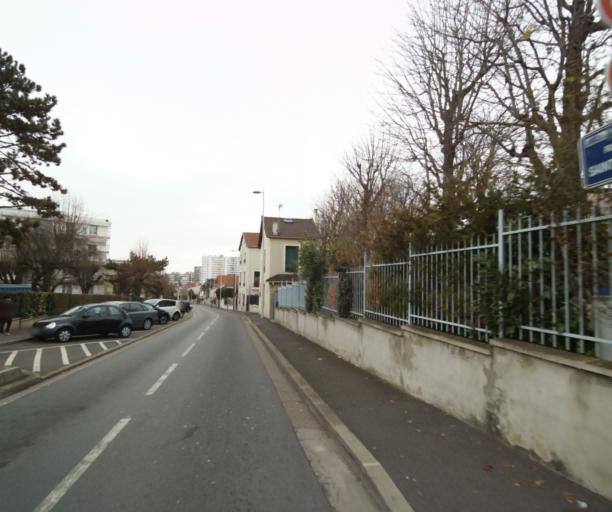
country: FR
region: Ile-de-France
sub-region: Departement des Hauts-de-Seine
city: Nanterre
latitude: 48.8835
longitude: 2.2013
